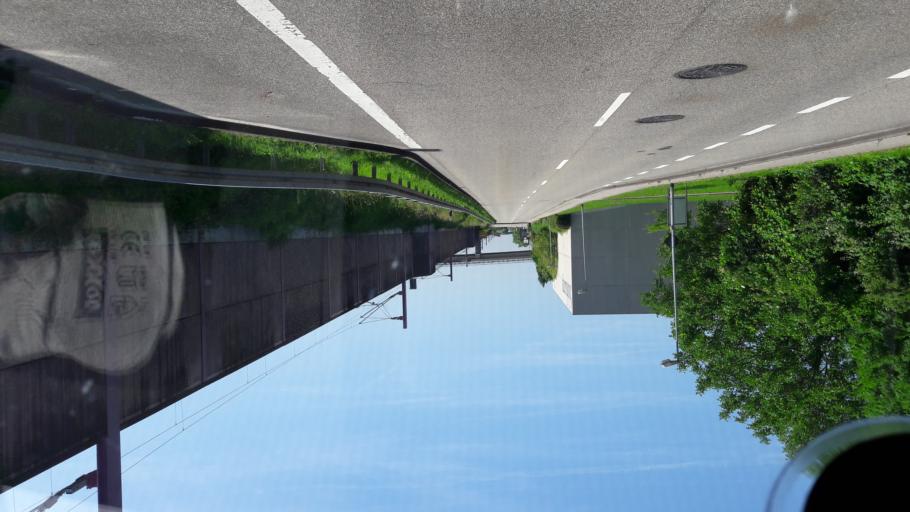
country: DE
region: Baden-Wuerttemberg
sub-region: Karlsruhe Region
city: Sinzheim
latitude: 48.7710
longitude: 8.1697
